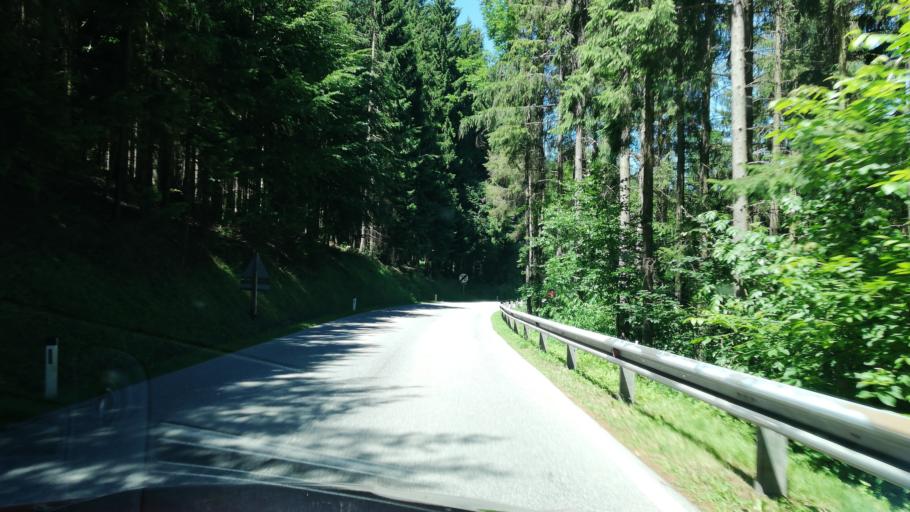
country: AT
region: Upper Austria
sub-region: Politischer Bezirk Urfahr-Umgebung
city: Haibach im Muhlkreis
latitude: 48.4382
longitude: 14.3570
